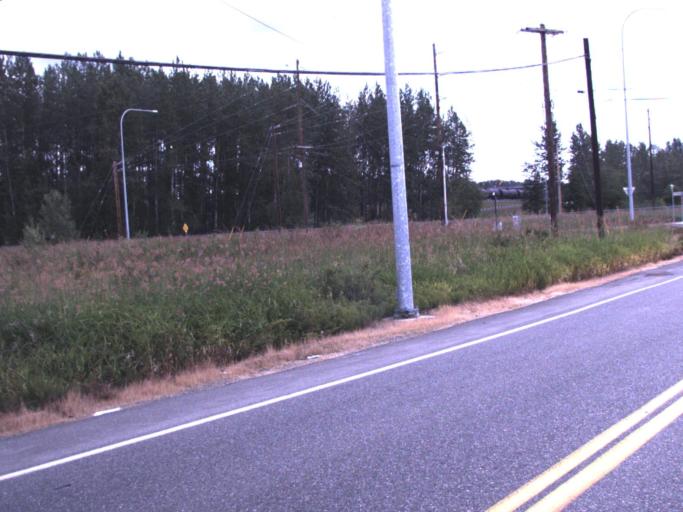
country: US
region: Washington
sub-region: Whatcom County
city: Birch Bay
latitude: 48.8927
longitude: -122.7265
